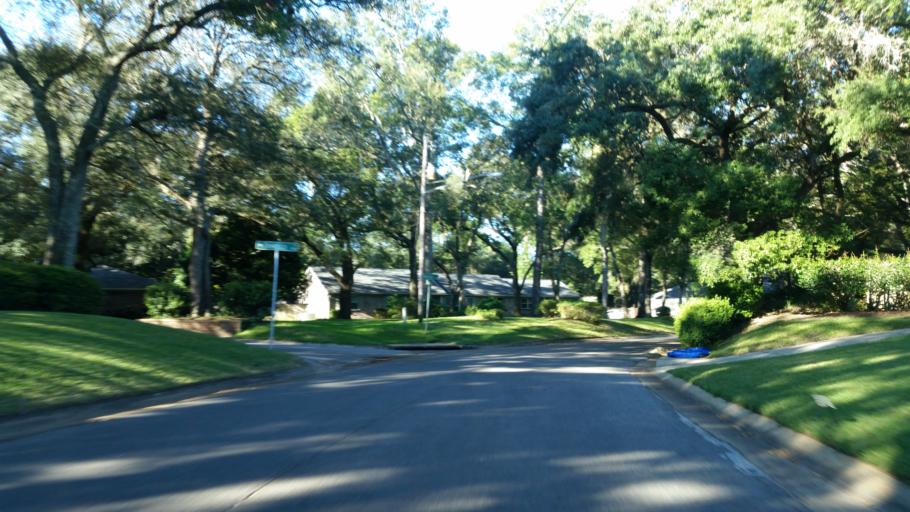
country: US
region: Florida
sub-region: Escambia County
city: East Pensacola Heights
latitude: 30.4678
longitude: -87.1652
